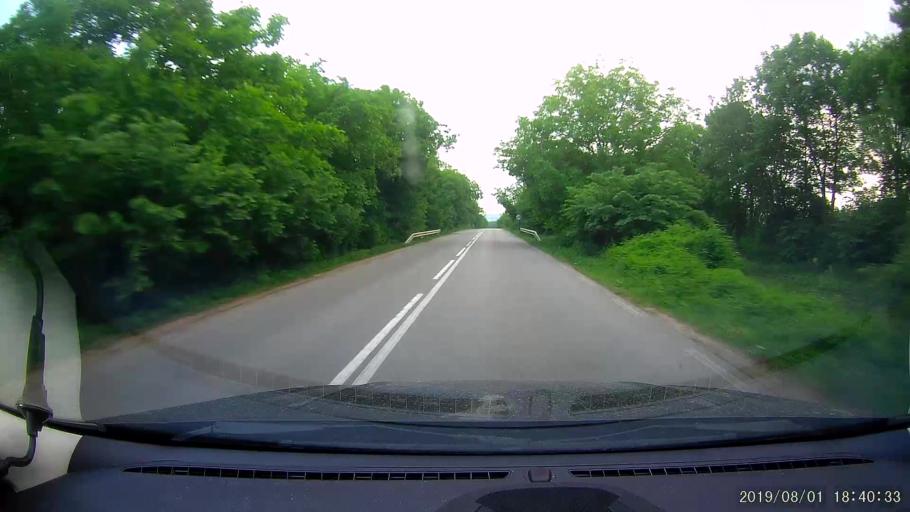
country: BG
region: Shumen
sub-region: Obshtina Khitrino
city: Gara Khitrino
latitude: 43.3646
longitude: 26.9197
